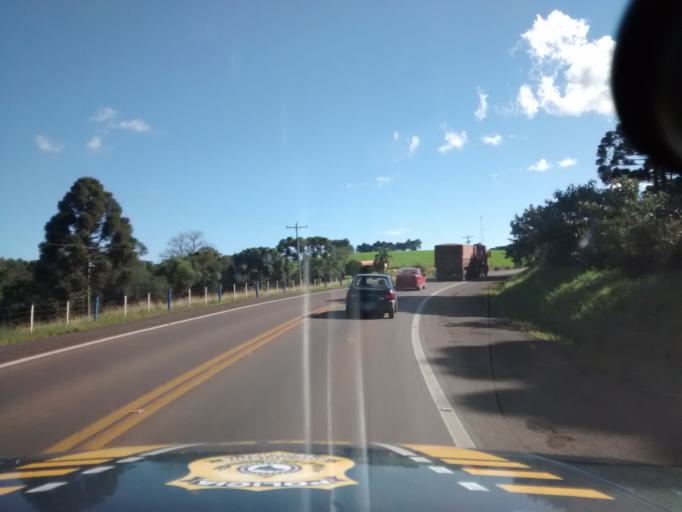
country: BR
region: Rio Grande do Sul
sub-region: Lagoa Vermelha
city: Lagoa Vermelha
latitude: -28.2985
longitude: -51.4511
